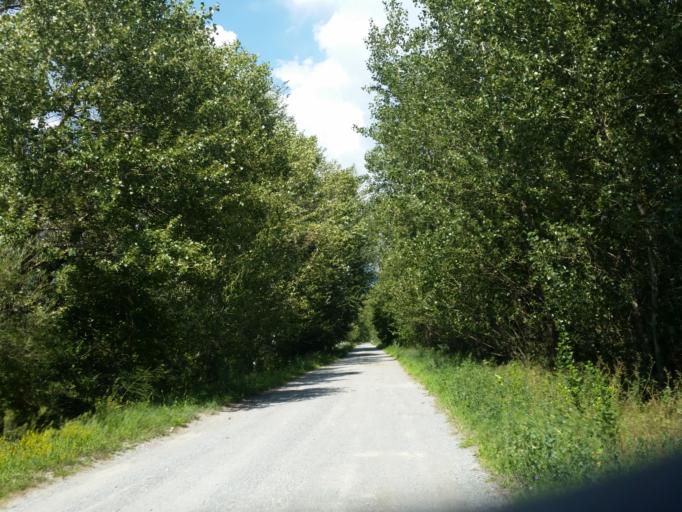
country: CH
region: Valais
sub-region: Martigny District
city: Saillon
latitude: 46.1634
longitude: 7.1981
